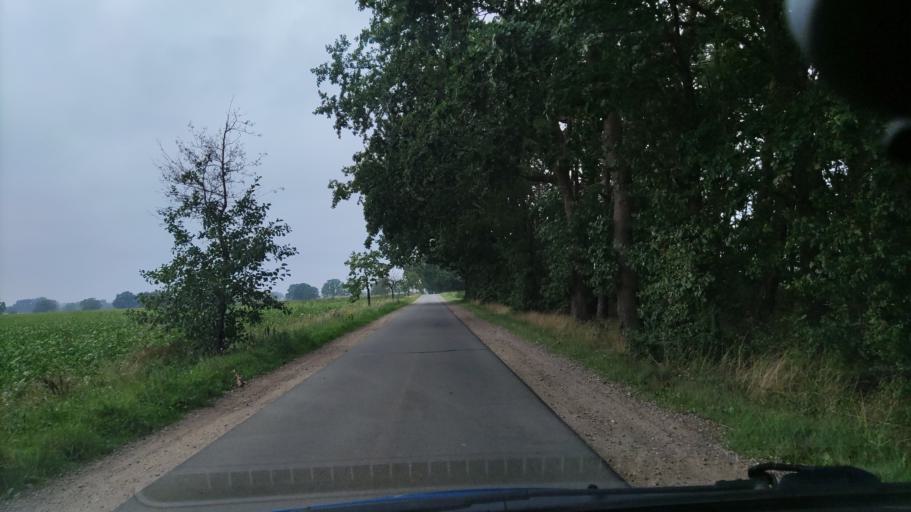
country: DE
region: Lower Saxony
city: Altenmedingen
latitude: 53.1229
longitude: 10.6255
